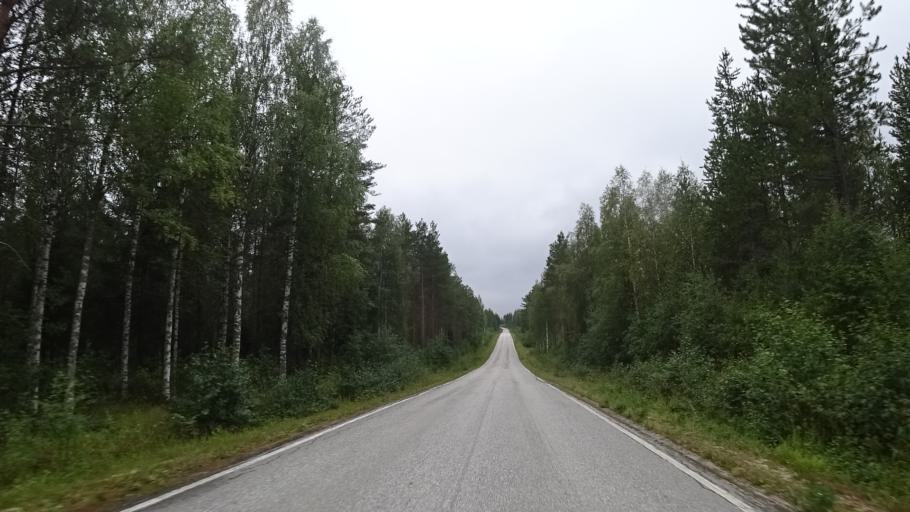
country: FI
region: North Karelia
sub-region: Pielisen Karjala
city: Lieksa
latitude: 63.3730
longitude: 30.3019
